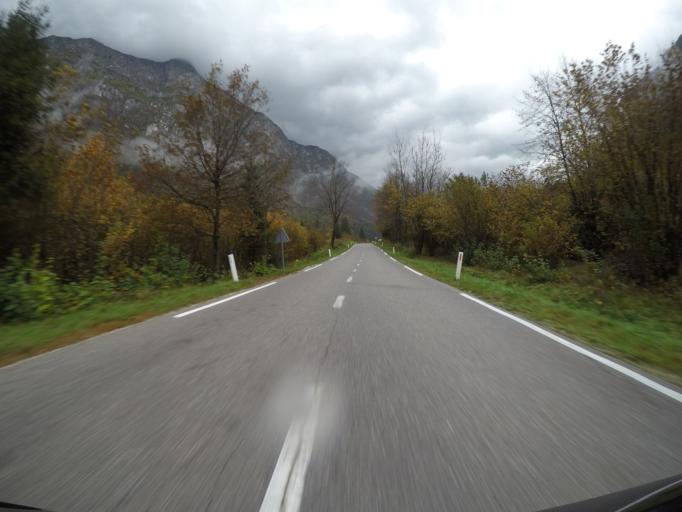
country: SI
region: Bovec
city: Bovec
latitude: 46.3357
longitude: 13.6415
